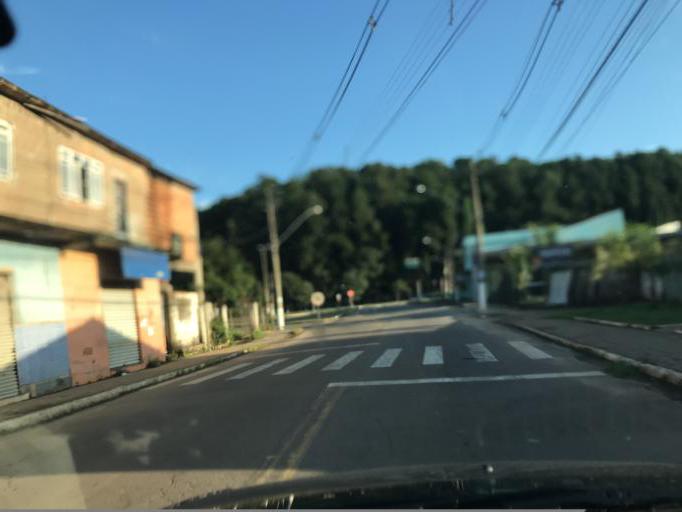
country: BR
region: Minas Gerais
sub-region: Tres Coracoes
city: Tres Coracoes
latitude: -21.7004
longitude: -45.2410
